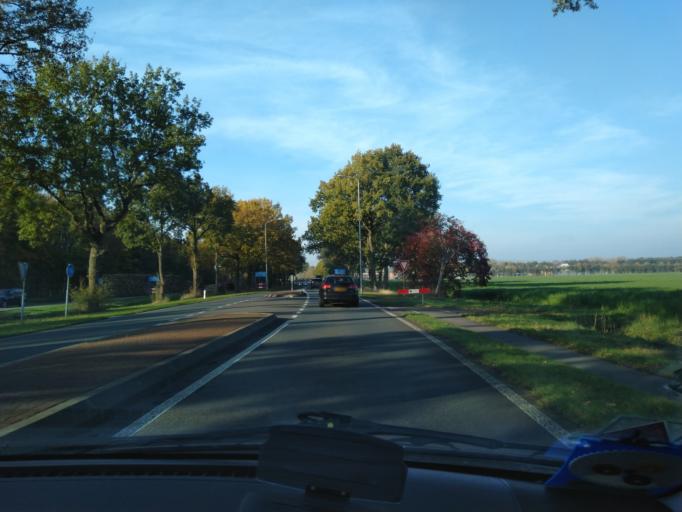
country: NL
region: Groningen
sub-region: Gemeente Hoogezand-Sappemeer
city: Hoogezand
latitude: 53.1452
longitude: 6.7661
